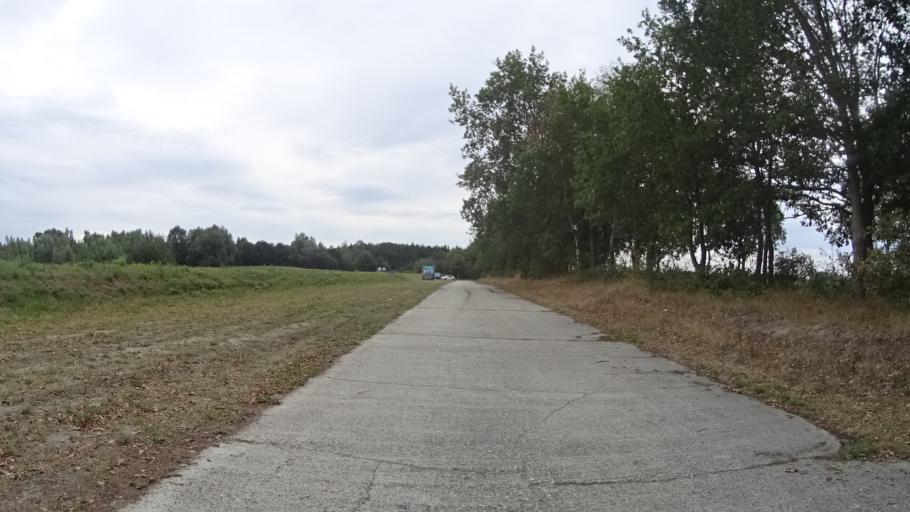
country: NL
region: Groningen
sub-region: Gemeente Slochteren
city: Slochteren
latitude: 53.1819
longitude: 6.8508
